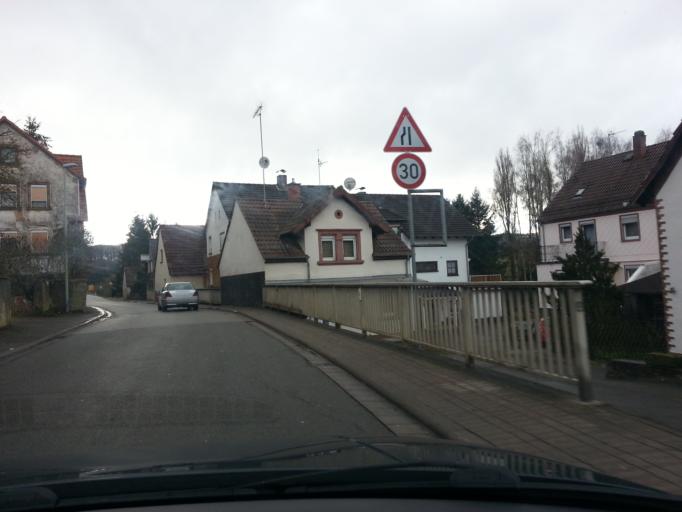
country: DE
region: Rheinland-Pfalz
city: Reichenbach-Steegen
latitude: 49.4988
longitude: 7.5467
